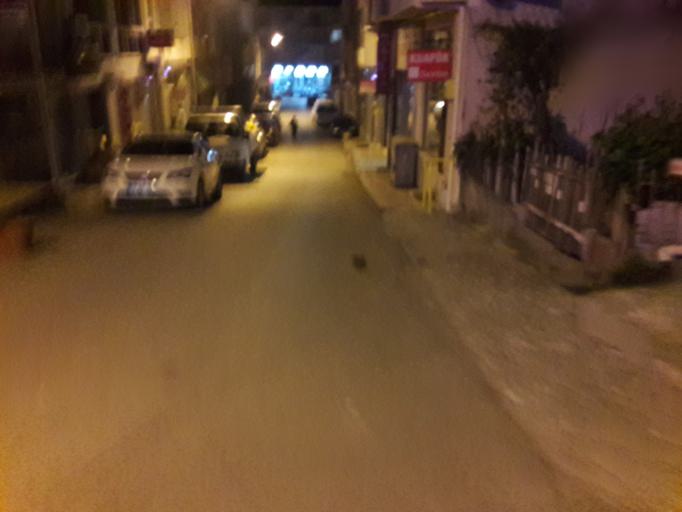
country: TR
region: Sinop
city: Sinop
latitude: 42.0258
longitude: 35.1468
